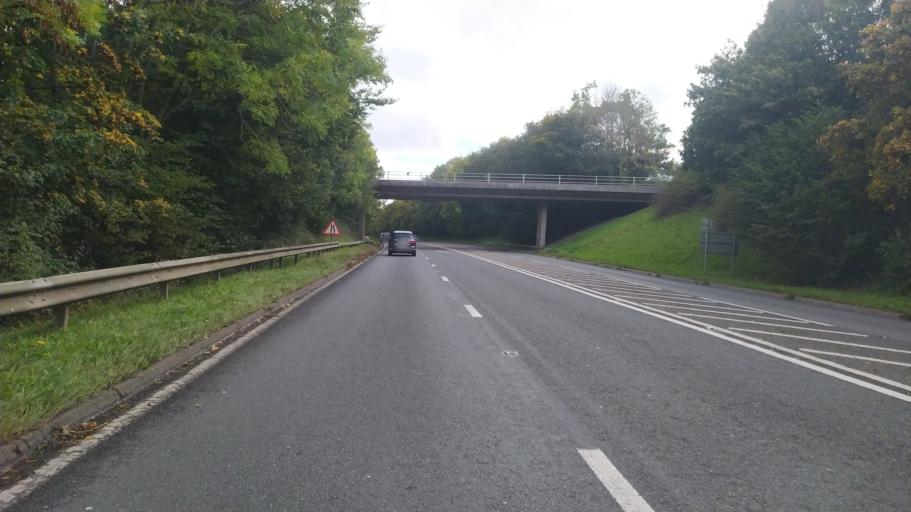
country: GB
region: England
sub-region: Dorset
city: Bridport
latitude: 50.7267
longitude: -2.7772
